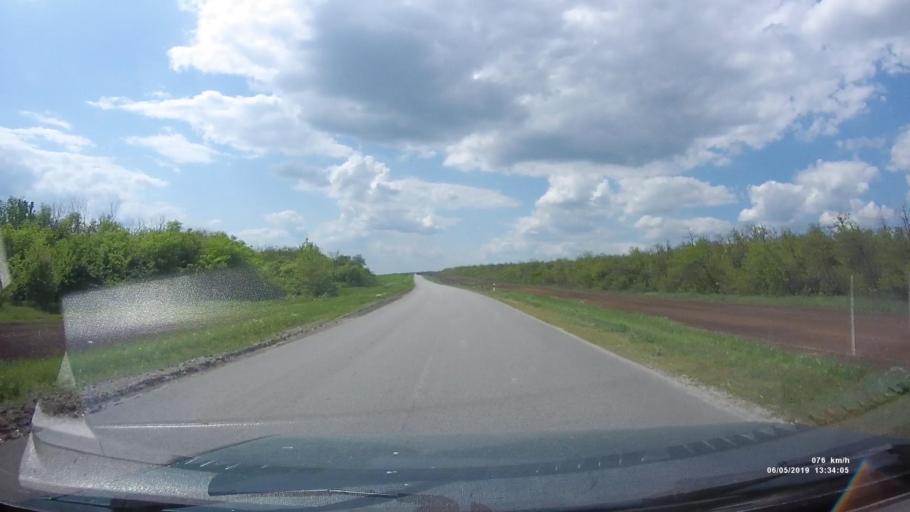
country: RU
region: Rostov
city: Ust'-Donetskiy
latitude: 47.6922
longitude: 40.7690
